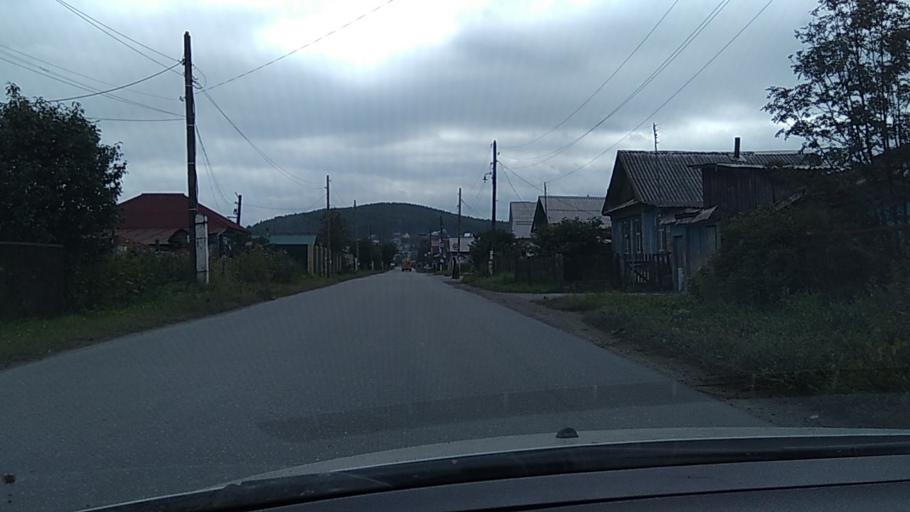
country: RU
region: Chelyabinsk
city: Zlatoust
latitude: 55.0872
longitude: 59.6901
